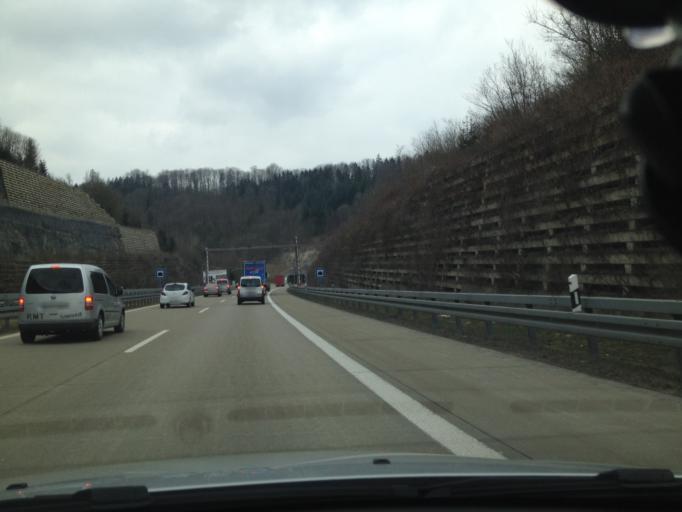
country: DE
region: Baden-Wuerttemberg
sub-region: Regierungsbezirk Stuttgart
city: Westhausen
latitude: 48.8675
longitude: 10.1773
